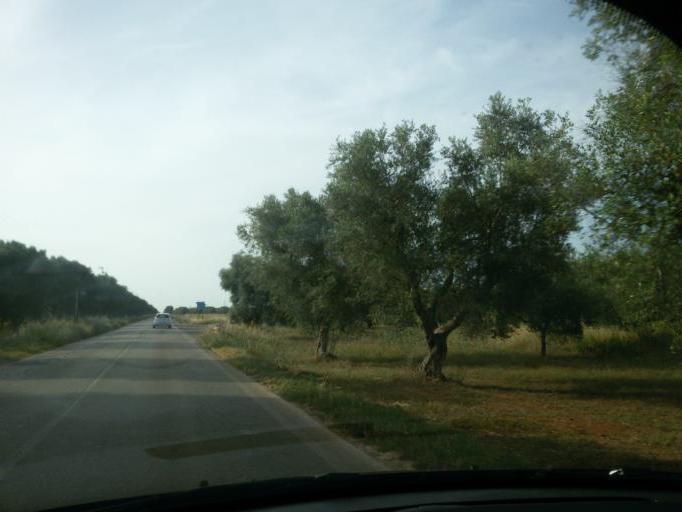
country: IT
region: Apulia
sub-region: Provincia di Brindisi
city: San Pancrazio Salentino
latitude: 40.3535
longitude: 17.8448
